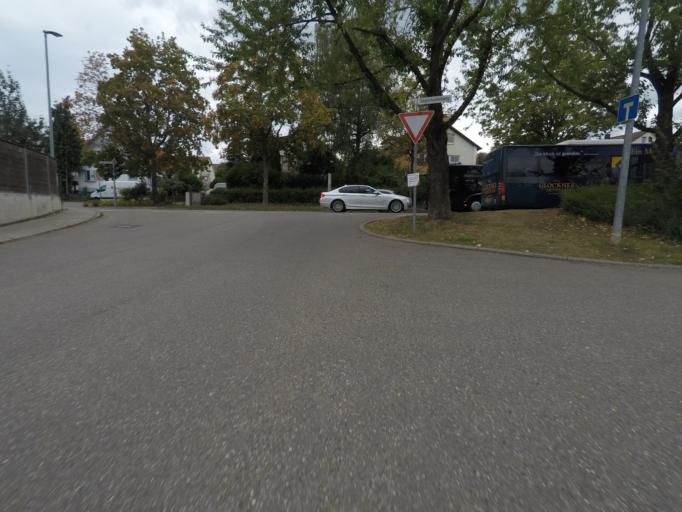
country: DE
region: Baden-Wuerttemberg
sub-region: Regierungsbezirk Stuttgart
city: Leinfelden-Echterdingen
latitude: 48.6705
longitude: 9.1748
